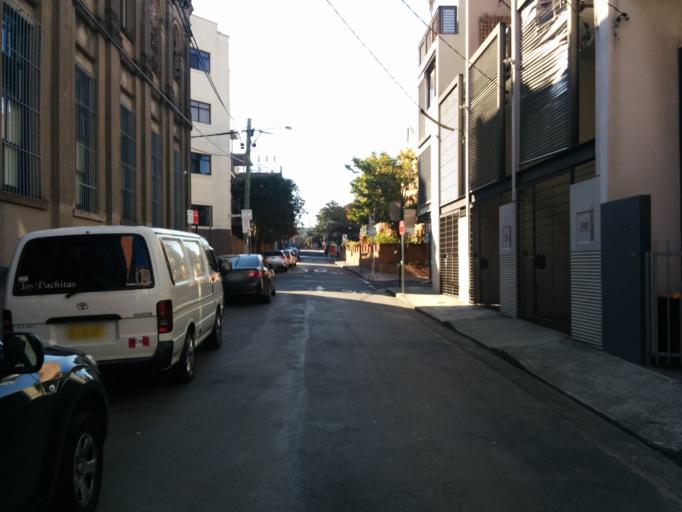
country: AU
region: New South Wales
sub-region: City of Sydney
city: Redfern
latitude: -33.8930
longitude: 151.2006
